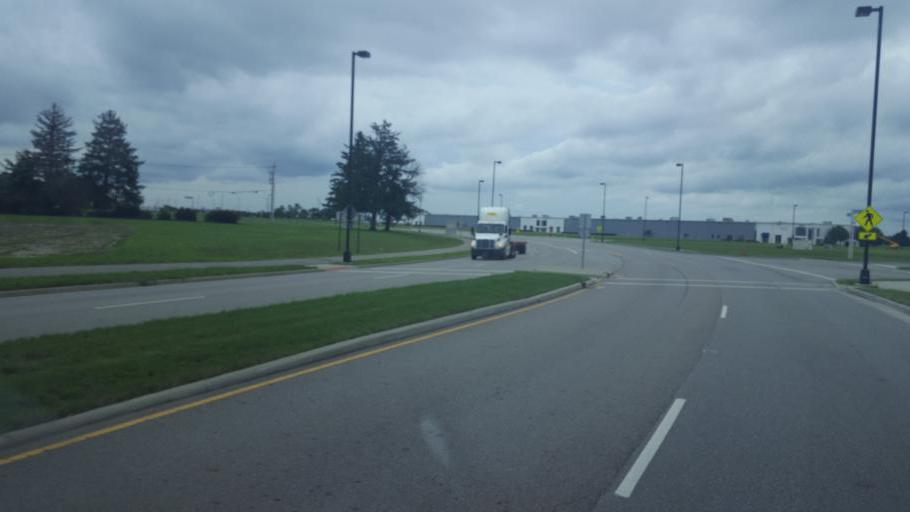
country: US
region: Ohio
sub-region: Franklin County
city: Obetz
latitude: 39.8232
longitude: -82.9343
